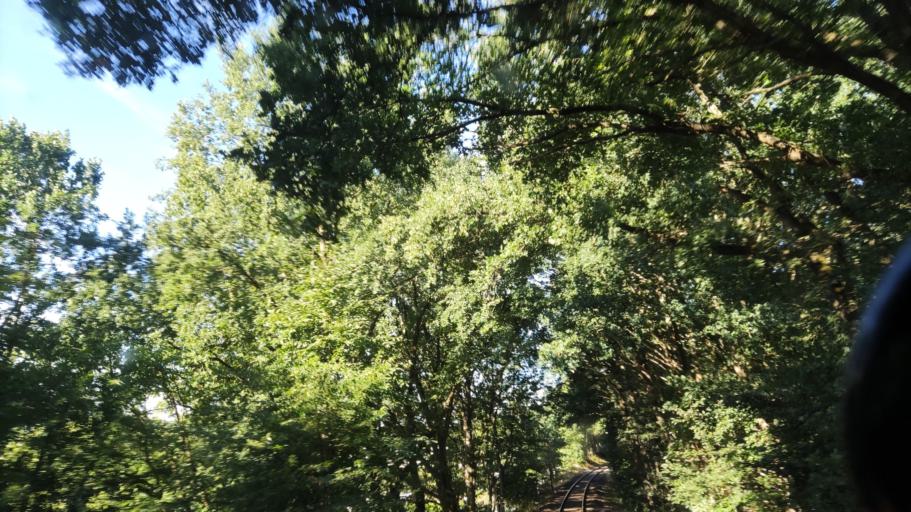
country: DE
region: Lower Saxony
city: Amelinghausen
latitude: 53.1266
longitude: 10.2305
